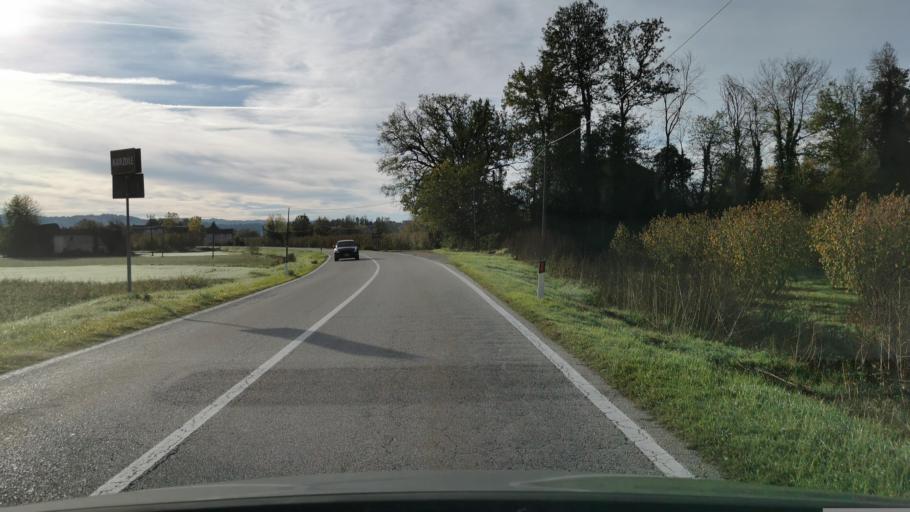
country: IT
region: Piedmont
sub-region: Provincia di Cuneo
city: Narzole
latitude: 44.5906
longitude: 7.8943
